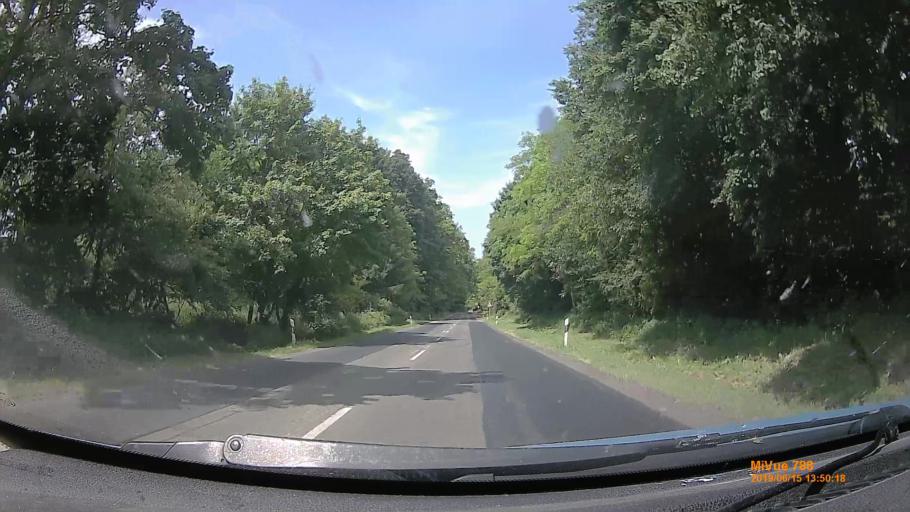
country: HU
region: Tolna
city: Iregszemcse
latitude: 46.7412
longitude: 18.1624
